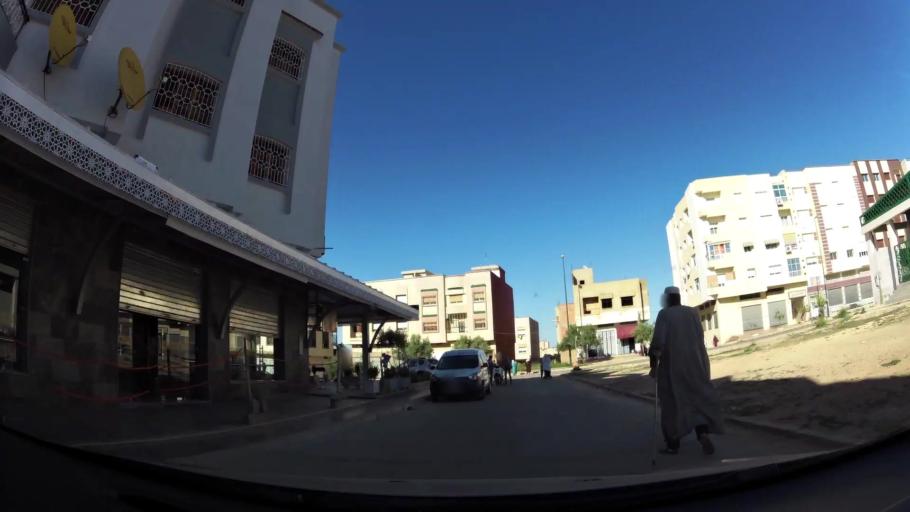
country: MA
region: Meknes-Tafilalet
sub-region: Meknes
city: Meknes
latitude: 33.8862
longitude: -5.4993
